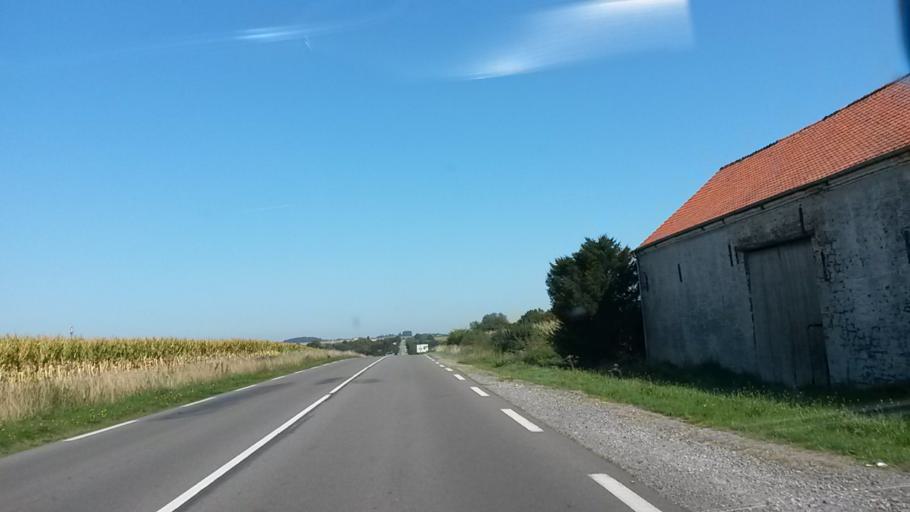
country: FR
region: Nord-Pas-de-Calais
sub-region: Departement du Nord
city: Hautmont
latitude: 50.2013
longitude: 3.9503
